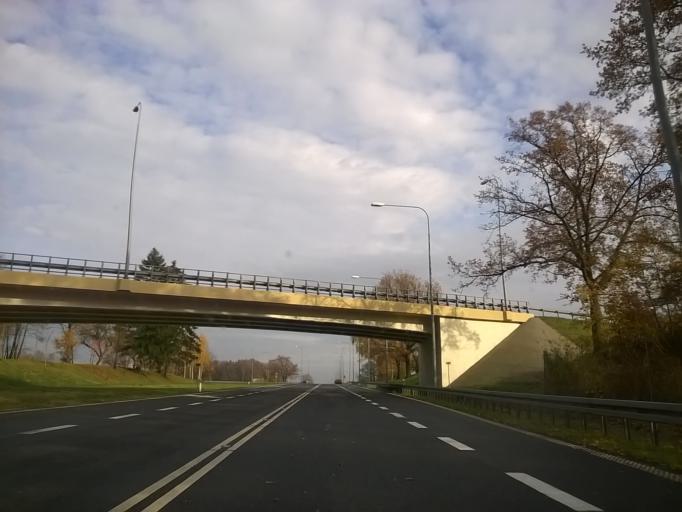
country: PL
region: Warmian-Masurian Voivodeship
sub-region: Powiat braniewski
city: Braniewo
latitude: 54.3552
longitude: 19.9219
